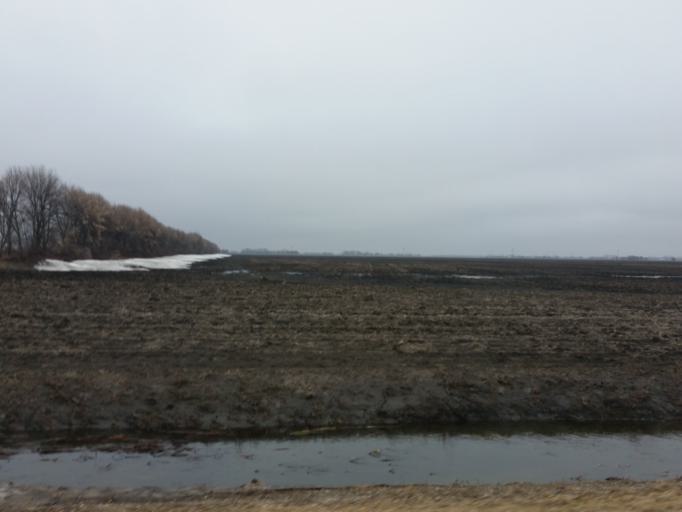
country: US
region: North Dakota
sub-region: Walsh County
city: Grafton
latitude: 48.3533
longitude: -97.1999
